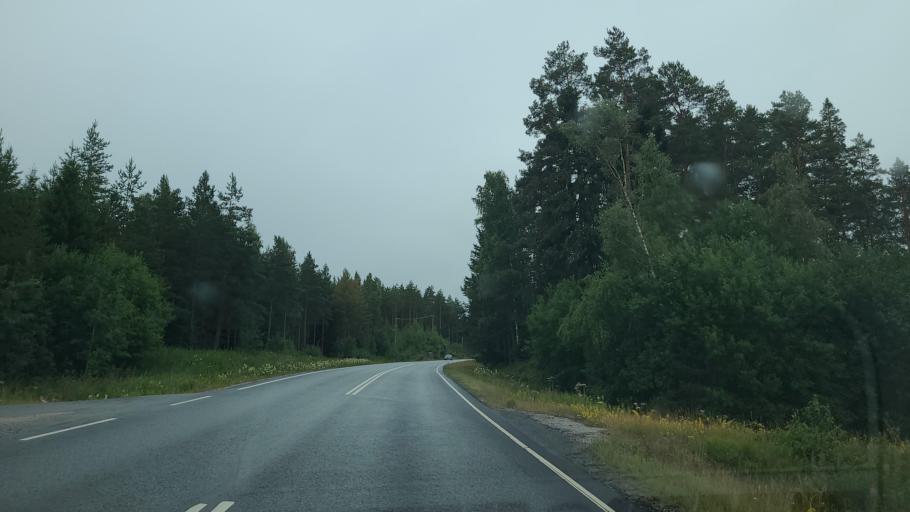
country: FI
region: Varsinais-Suomi
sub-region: Turku
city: Sauvo
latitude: 60.2727
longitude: 22.6693
